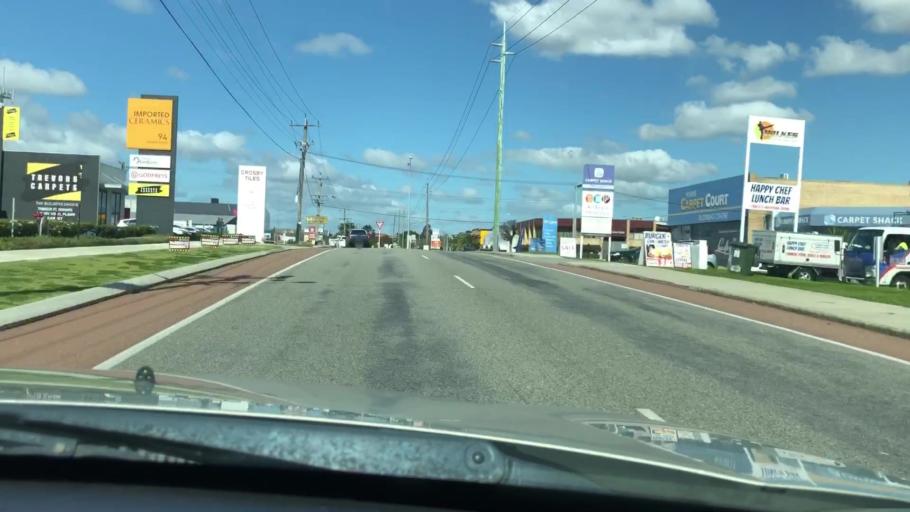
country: AU
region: Western Australia
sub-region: Melville
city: Myaree
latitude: -32.0426
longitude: 115.8223
